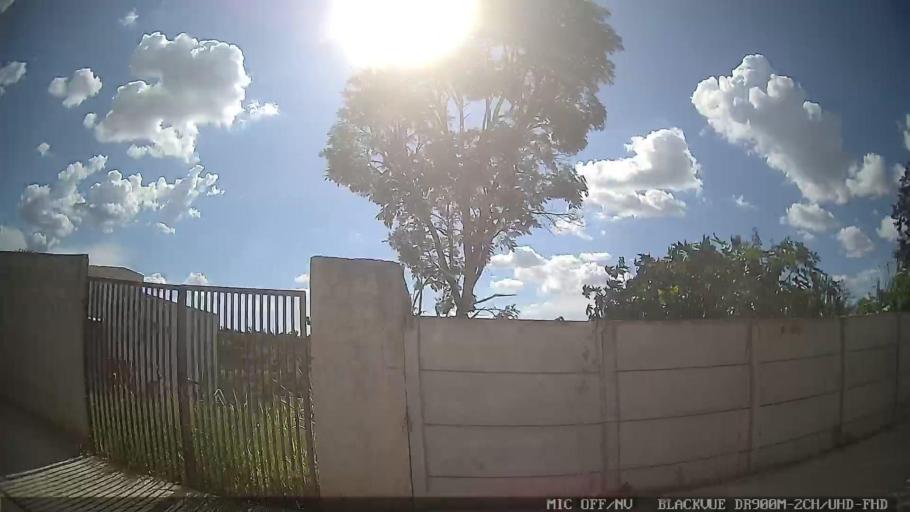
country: BR
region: Sao Paulo
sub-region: Atibaia
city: Atibaia
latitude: -23.1135
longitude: -46.5223
